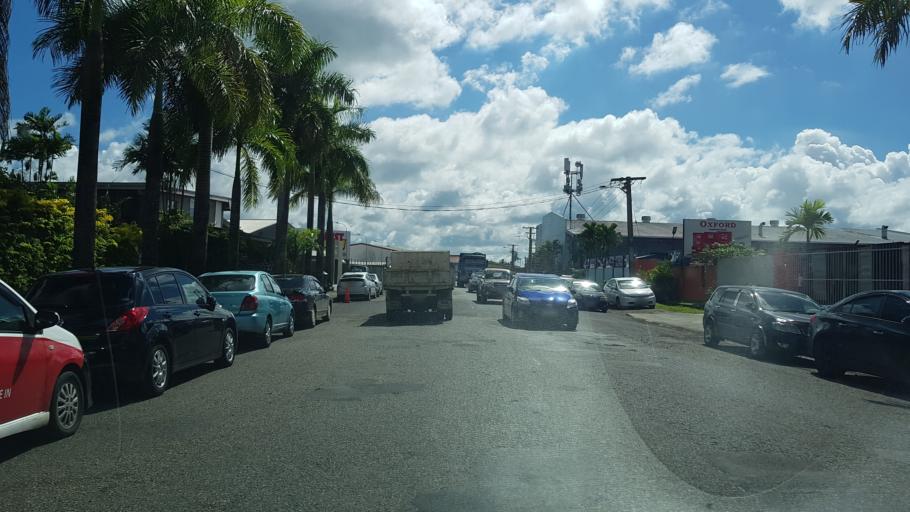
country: FJ
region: Central
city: Suva
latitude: -18.1277
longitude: 178.4553
